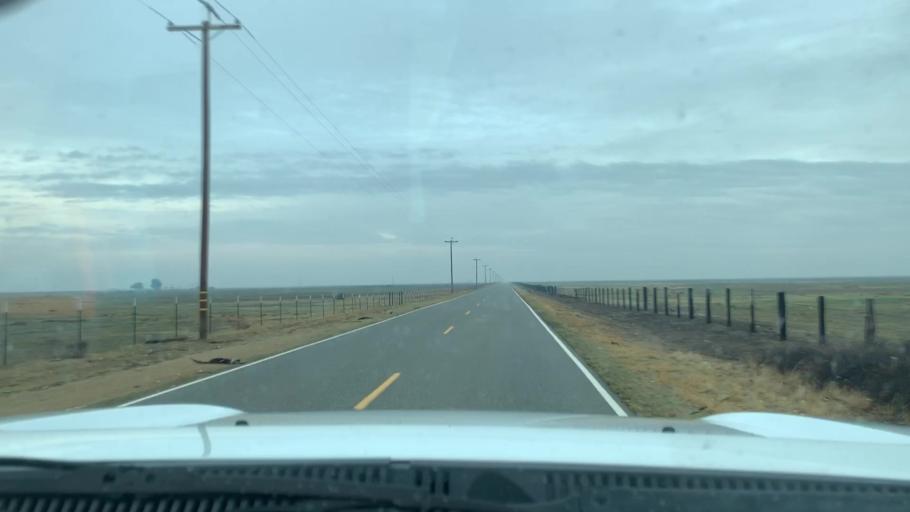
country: US
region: California
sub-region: Kern County
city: Lost Hills
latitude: 35.6742
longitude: -119.5799
